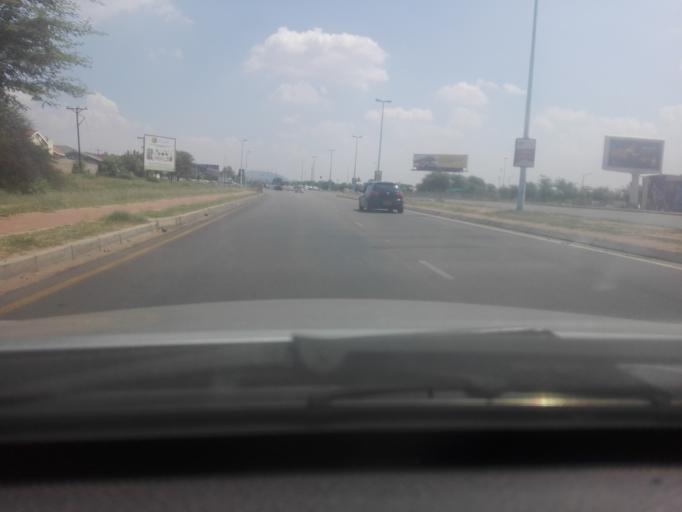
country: BW
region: South East
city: Gaborone
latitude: -24.6439
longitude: 25.8862
